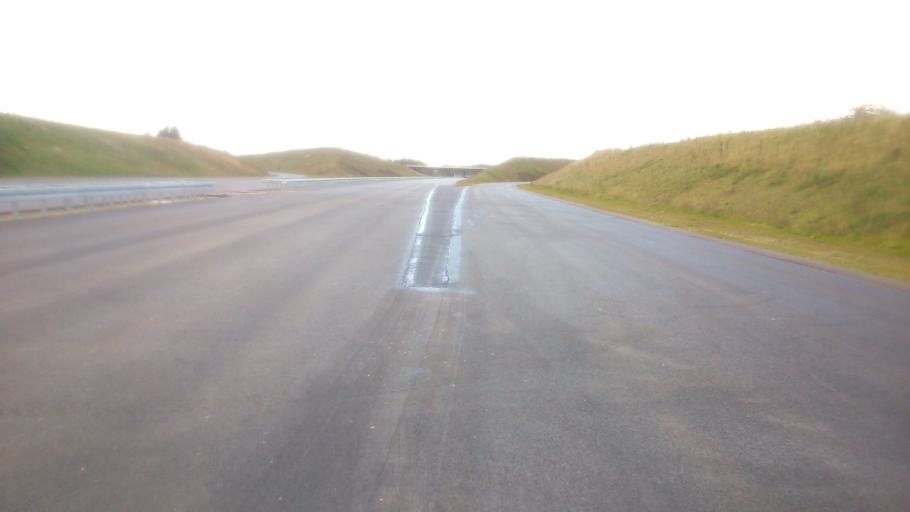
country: DK
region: Central Jutland
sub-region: Silkeborg Kommune
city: Silkeborg
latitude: 56.1983
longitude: 9.5080
